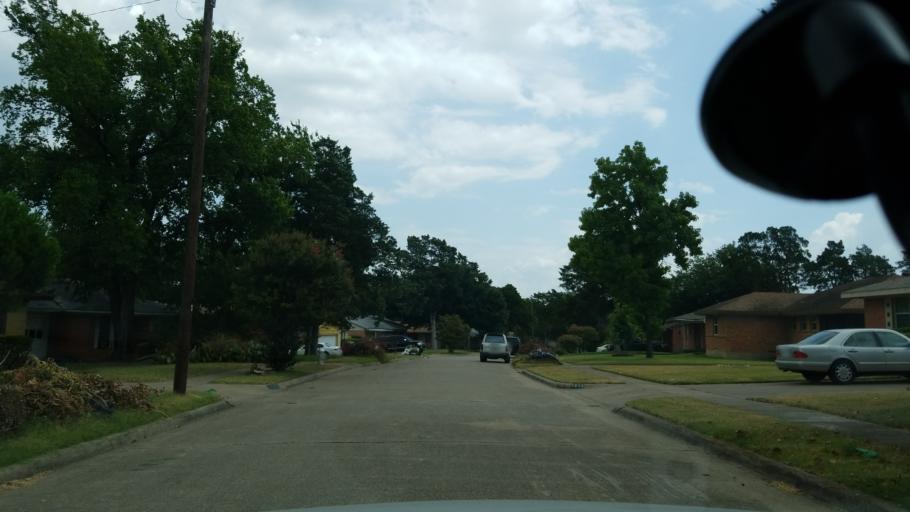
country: US
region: Texas
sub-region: Dallas County
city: Cockrell Hill
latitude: 32.6878
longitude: -96.8519
